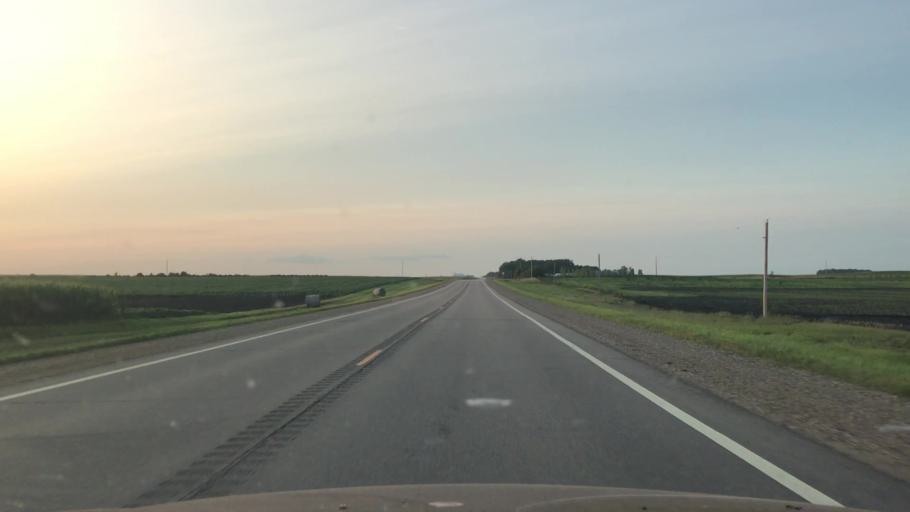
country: US
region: Minnesota
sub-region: Redwood County
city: Redwood Falls
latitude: 44.4381
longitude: -95.1176
